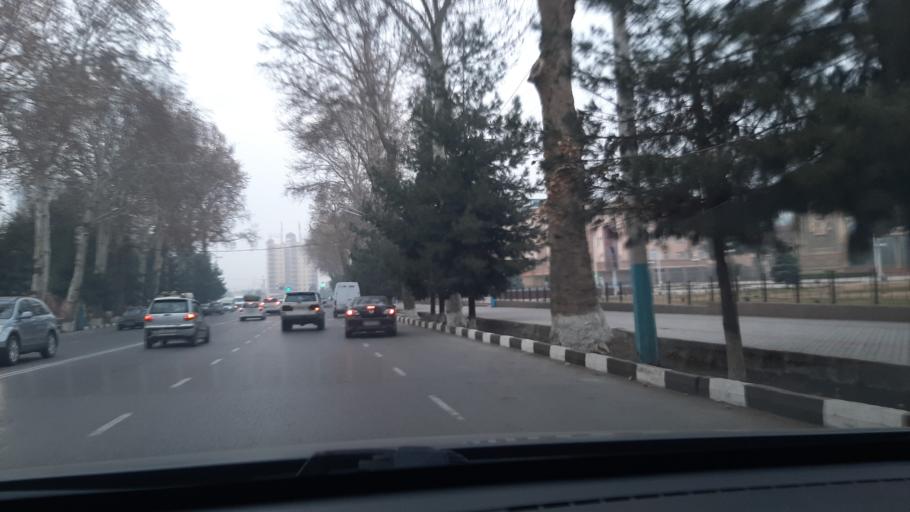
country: TJ
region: Viloyati Sughd
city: Khujand
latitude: 40.2697
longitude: 69.6461
